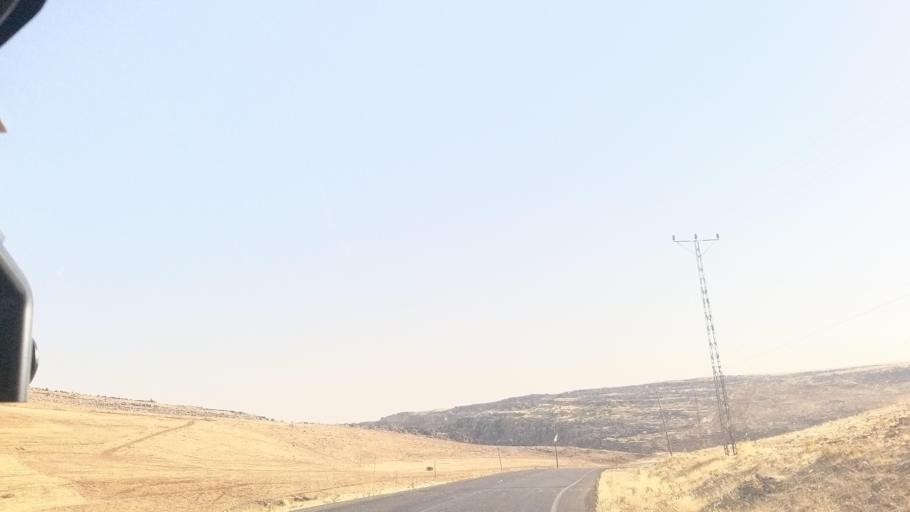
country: TR
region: Diyarbakir
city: Silvan
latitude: 38.1715
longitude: 41.0047
